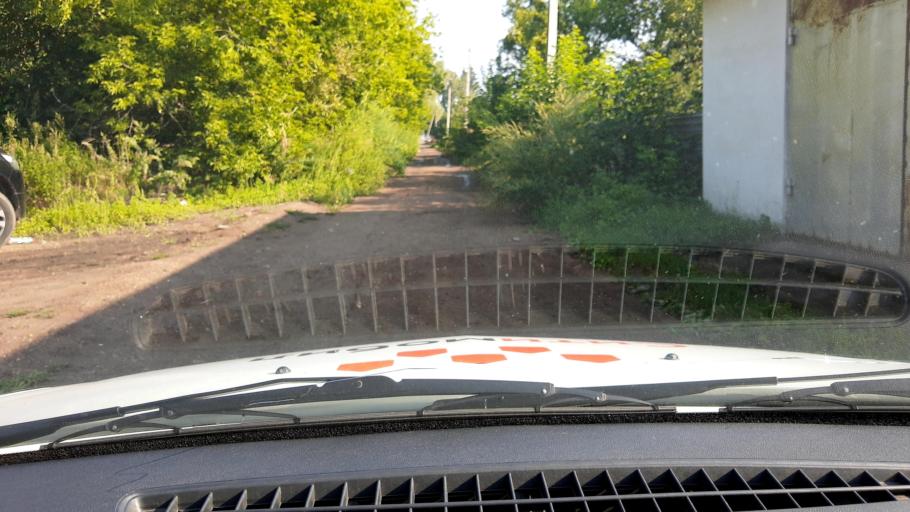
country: RU
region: Bashkortostan
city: Mikhaylovka
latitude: 54.6905
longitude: 55.8495
